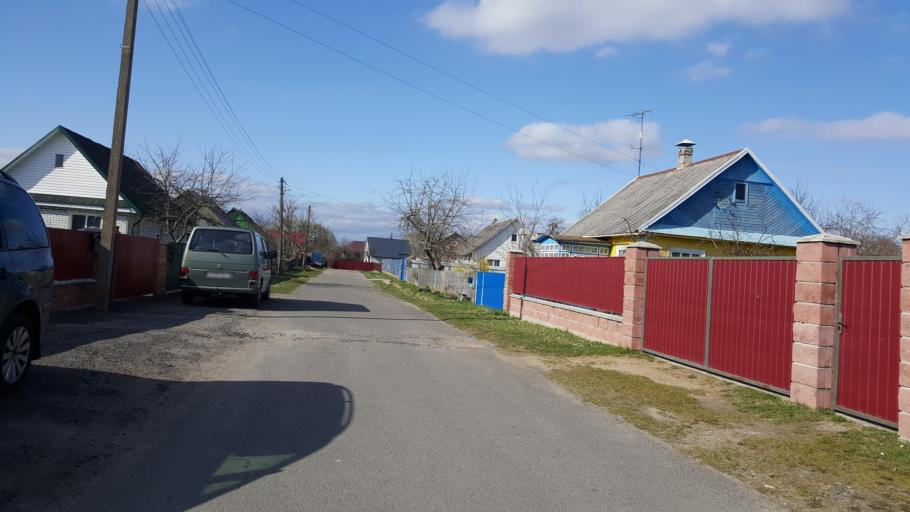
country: BY
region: Brest
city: Kamyanyets
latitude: 52.4023
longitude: 23.8143
